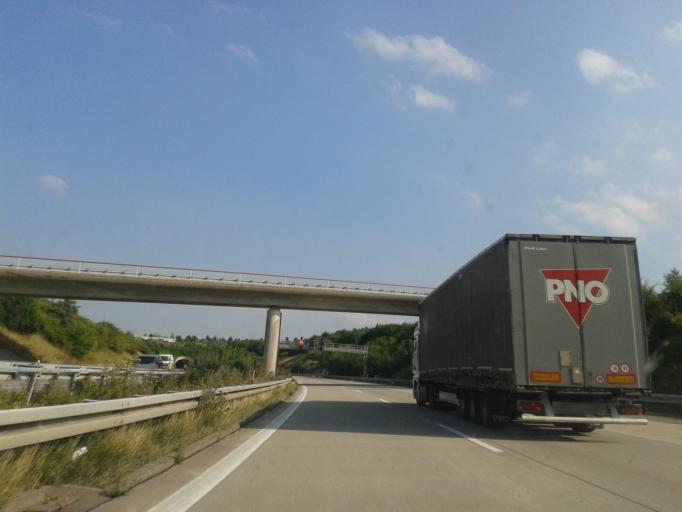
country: DE
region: Saxony
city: Freital
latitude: 51.0308
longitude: 13.6703
